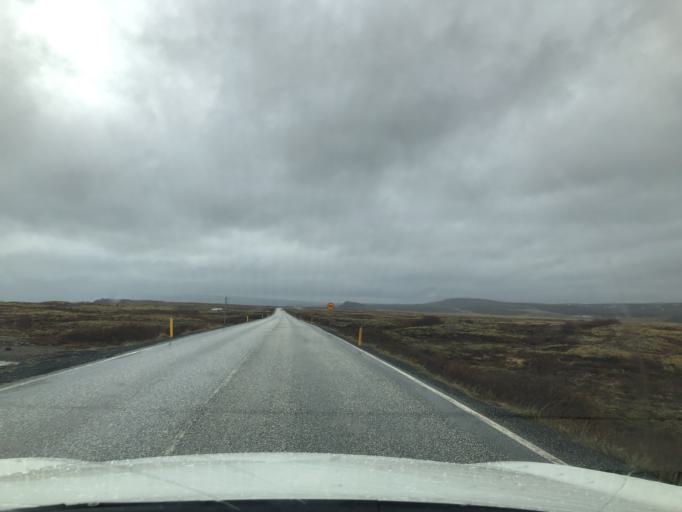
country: IS
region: South
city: Hveragerdi
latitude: 64.2760
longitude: -21.1054
